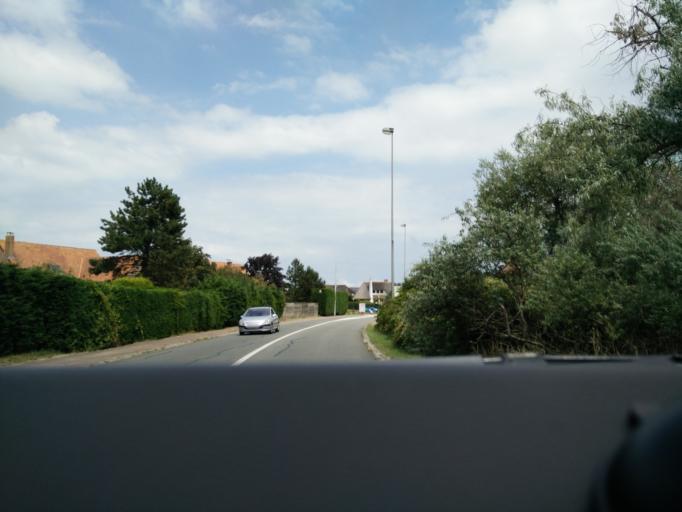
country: FR
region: Nord-Pas-de-Calais
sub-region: Departement du Nord
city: Bray-Dunes
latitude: 51.0741
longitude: 2.5108
